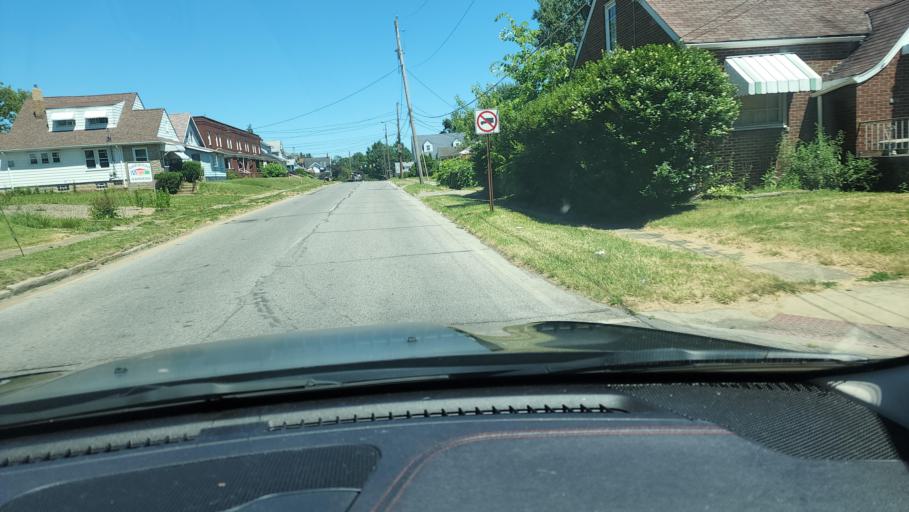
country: US
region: Ohio
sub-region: Trumbull County
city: Girard
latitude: 41.1050
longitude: -80.7000
